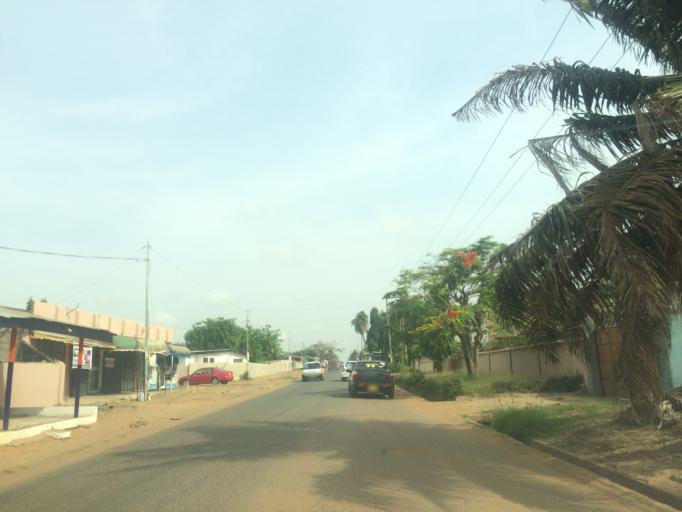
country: GH
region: Greater Accra
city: Nungua
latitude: 5.5958
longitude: -0.0894
